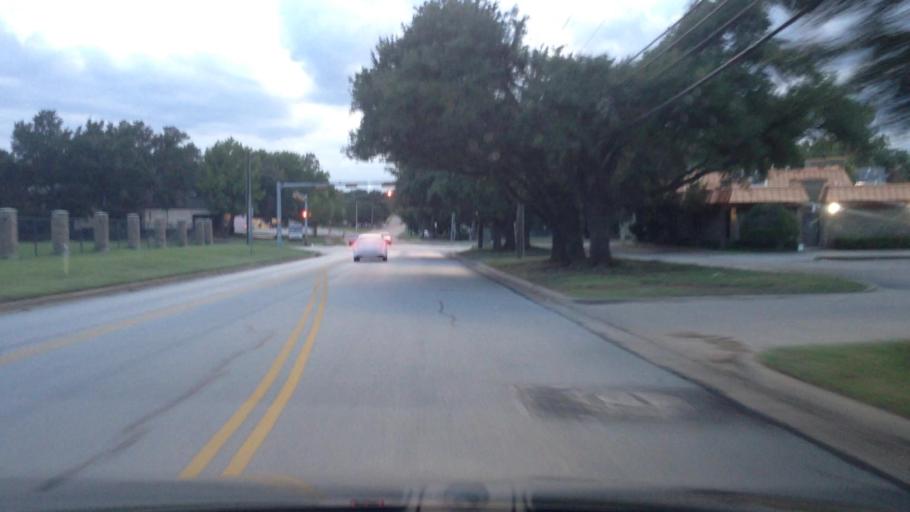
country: US
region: Texas
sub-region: Tarrant County
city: Arlington
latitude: 32.7429
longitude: -97.1307
